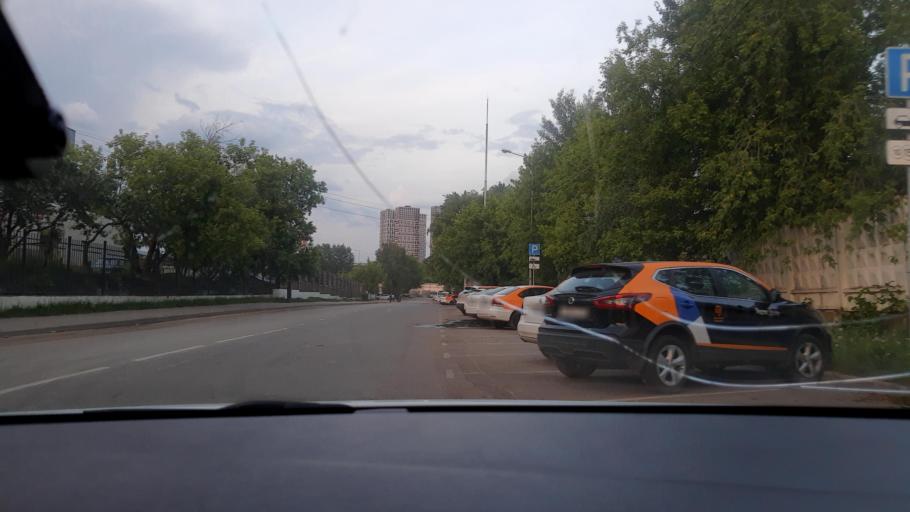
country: RU
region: Moskovskaya
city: Bogorodskoye
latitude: 55.8089
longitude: 37.7401
